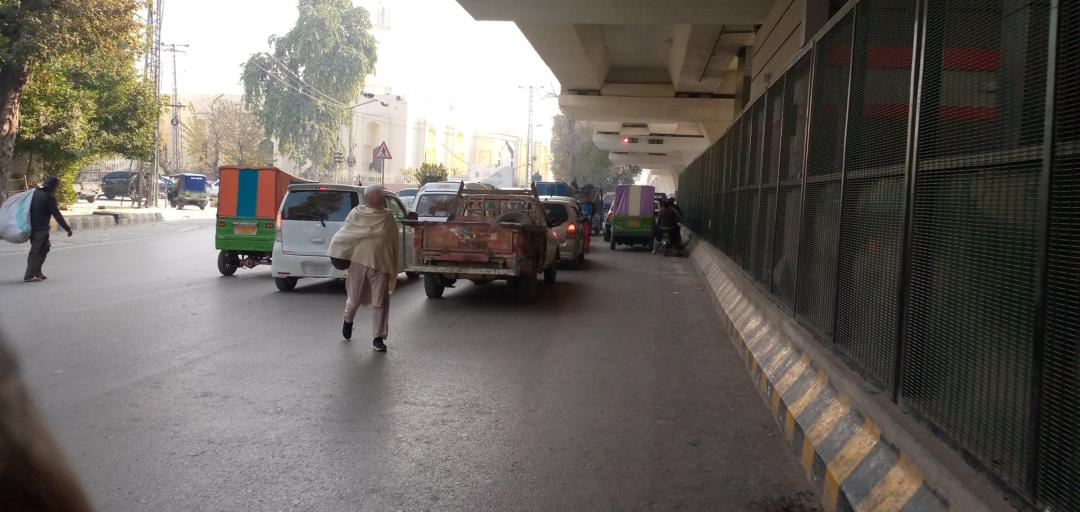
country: PK
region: Khyber Pakhtunkhwa
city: Peshawar
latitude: 33.9986
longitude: 71.5335
